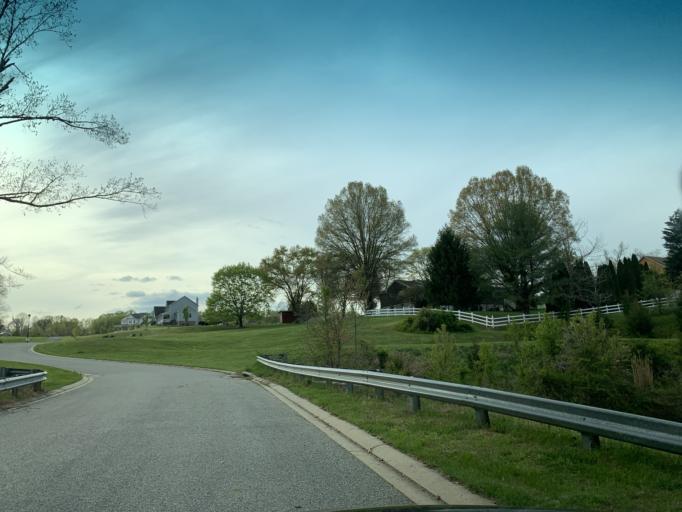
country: US
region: Maryland
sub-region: Harford County
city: Joppatowne
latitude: 39.4895
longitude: -76.3621
